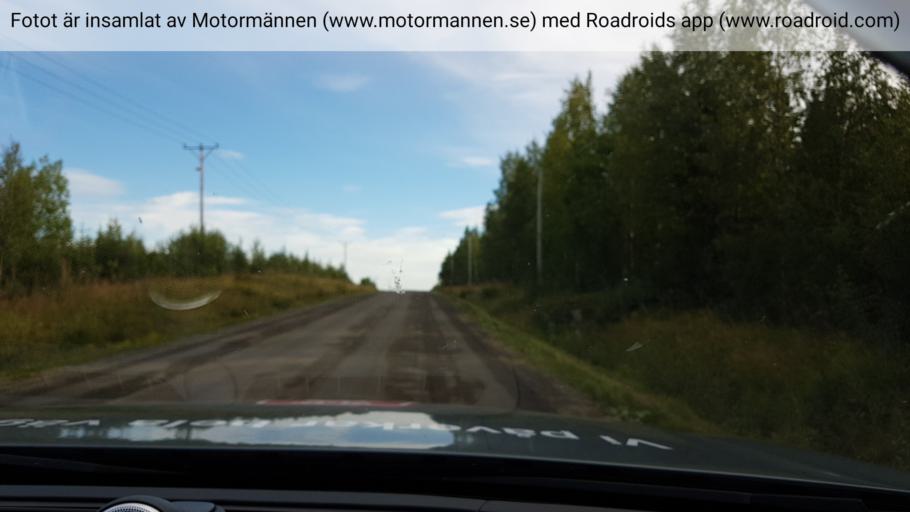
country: SE
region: Jaemtland
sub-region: Stroemsunds Kommun
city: Stroemsund
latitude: 63.9951
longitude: 15.8160
